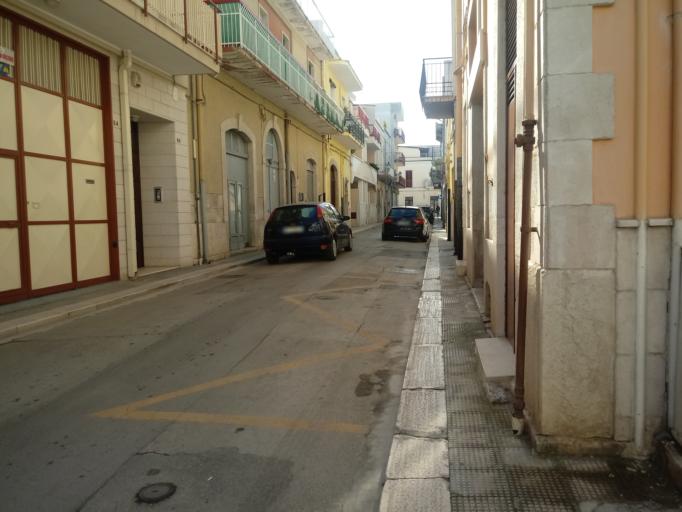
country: IT
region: Apulia
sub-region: Provincia di Barletta - Andria - Trani
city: Andria
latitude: 41.2221
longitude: 16.2963
